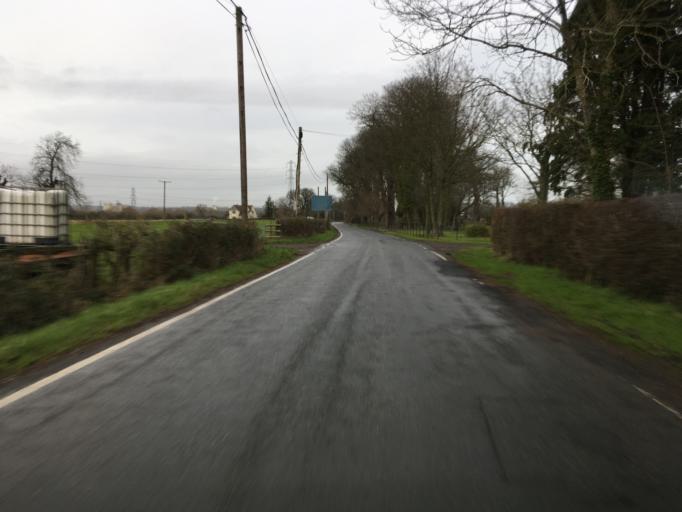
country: GB
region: Wales
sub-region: Newport
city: Goldcliff
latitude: 51.5568
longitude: -2.9096
